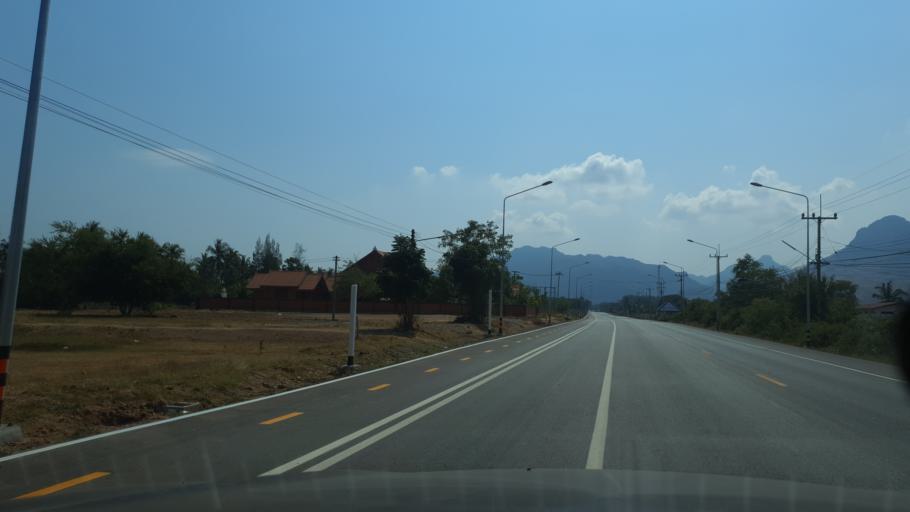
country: TH
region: Prachuap Khiri Khan
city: Sam Roi Yot
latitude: 12.2627
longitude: 99.9662
